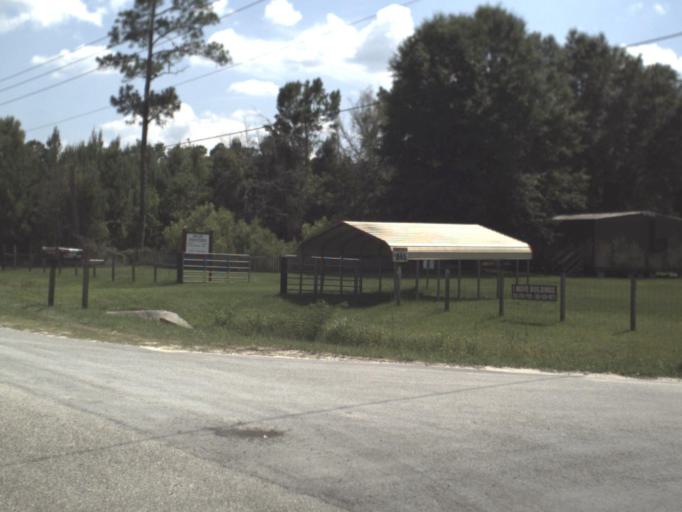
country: US
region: Florida
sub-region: Alachua County
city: Waldo
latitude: 29.8021
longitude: -82.1678
